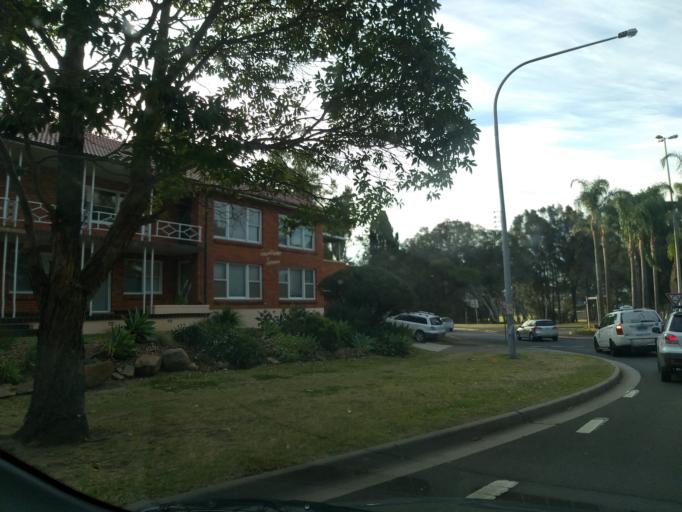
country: AU
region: New South Wales
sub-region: Wollongong
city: Wollongong
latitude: -34.4133
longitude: 150.8998
